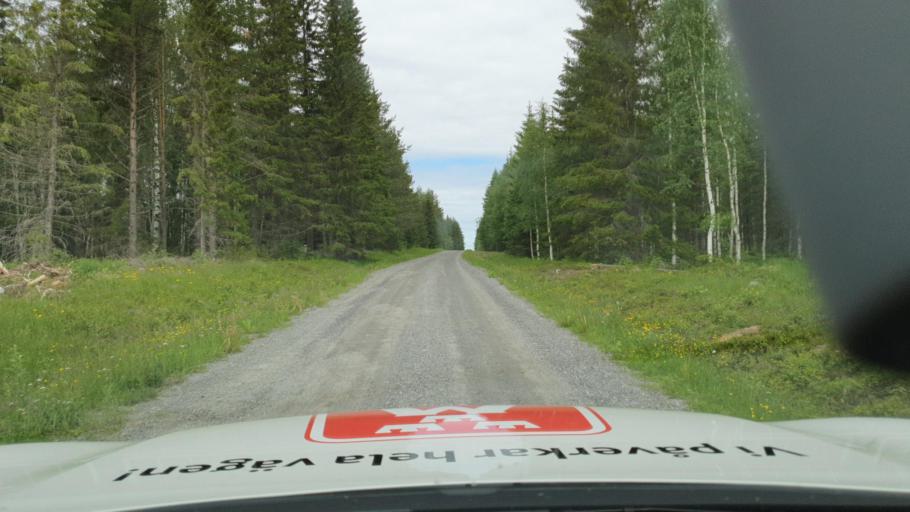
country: SE
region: Vaesterbotten
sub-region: Skelleftea Kommun
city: Langsele
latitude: 64.4593
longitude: 20.2827
